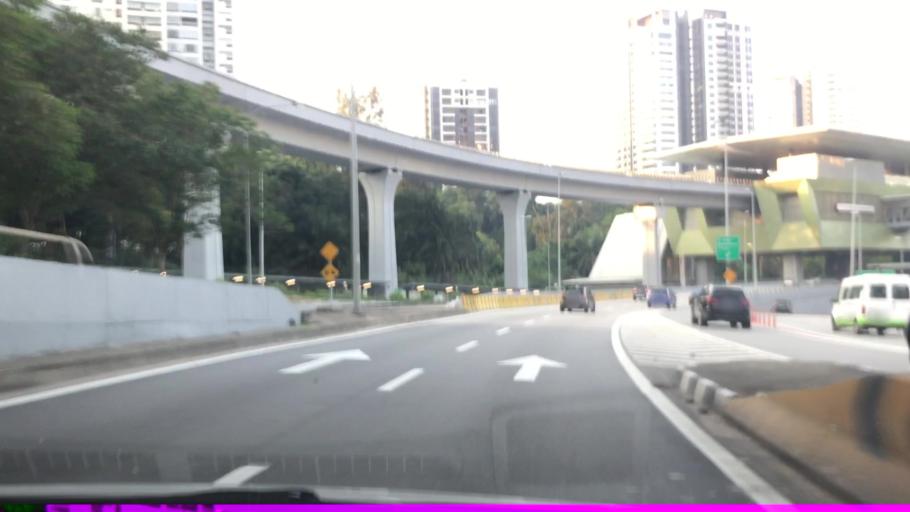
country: MY
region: Kuala Lumpur
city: Kuala Lumpur
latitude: 3.1448
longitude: 101.6638
